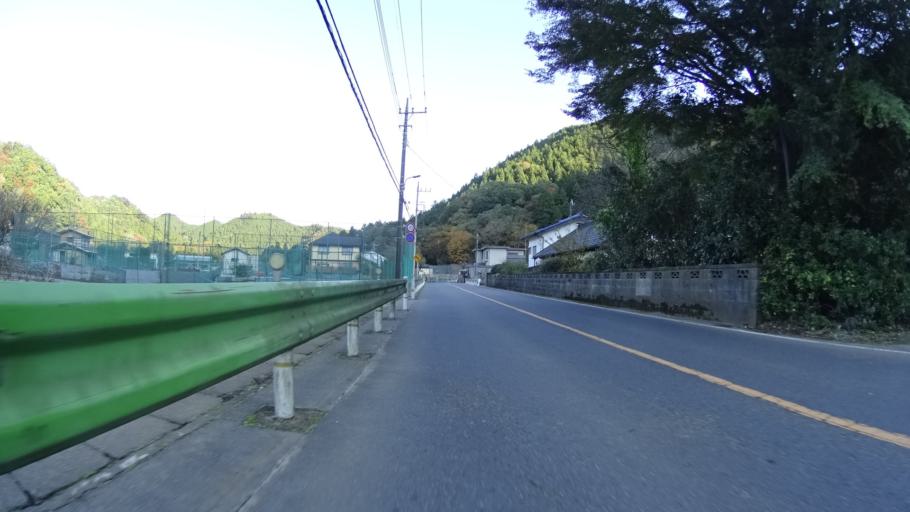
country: JP
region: Tokyo
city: Itsukaichi
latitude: 35.6716
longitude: 139.2248
